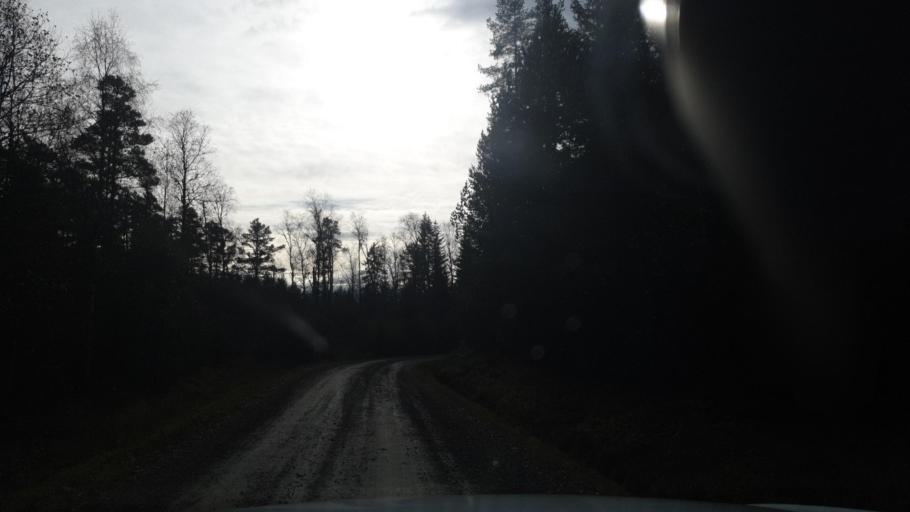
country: SE
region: Vaermland
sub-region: Eda Kommun
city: Charlottenberg
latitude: 59.9094
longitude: 12.3816
